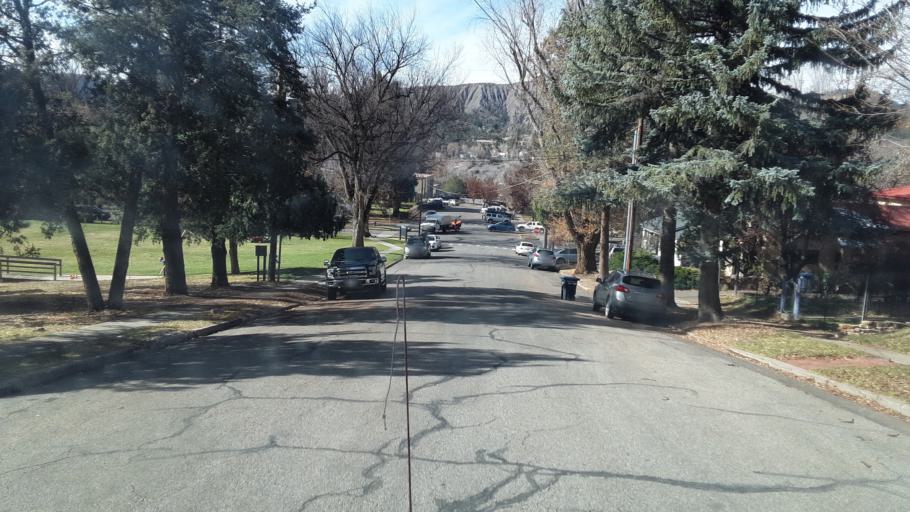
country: US
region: Colorado
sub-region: La Plata County
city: Durango
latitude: 37.2769
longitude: -107.8753
